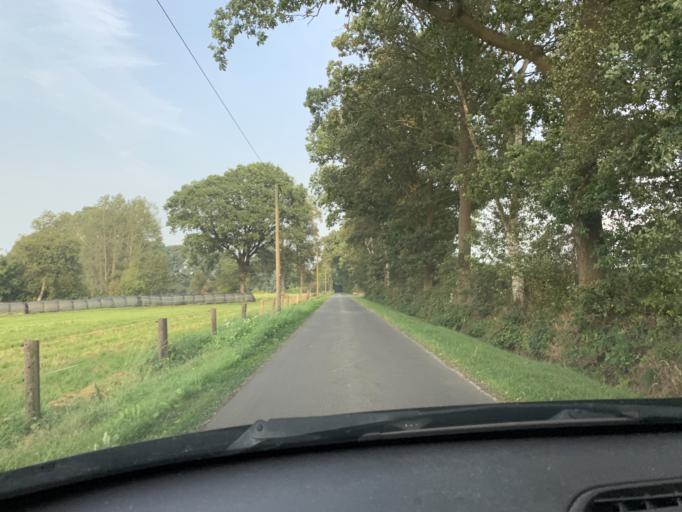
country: DE
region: Lower Saxony
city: Apen
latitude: 53.2481
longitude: 7.8312
